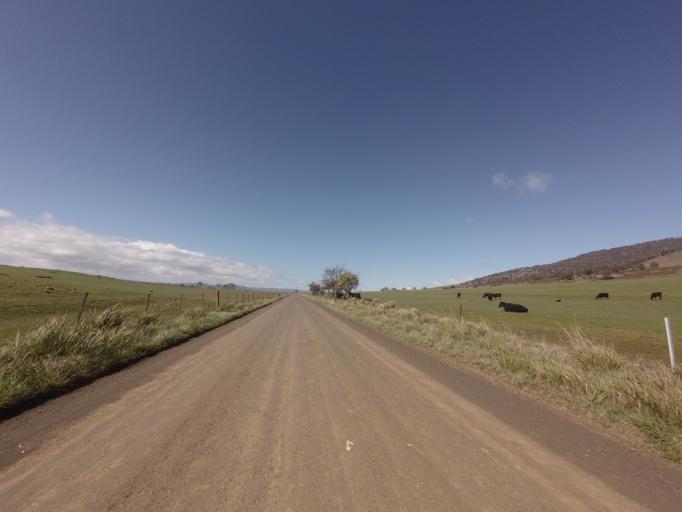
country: AU
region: Tasmania
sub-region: Northern Midlands
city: Evandale
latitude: -41.9203
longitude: 147.3977
